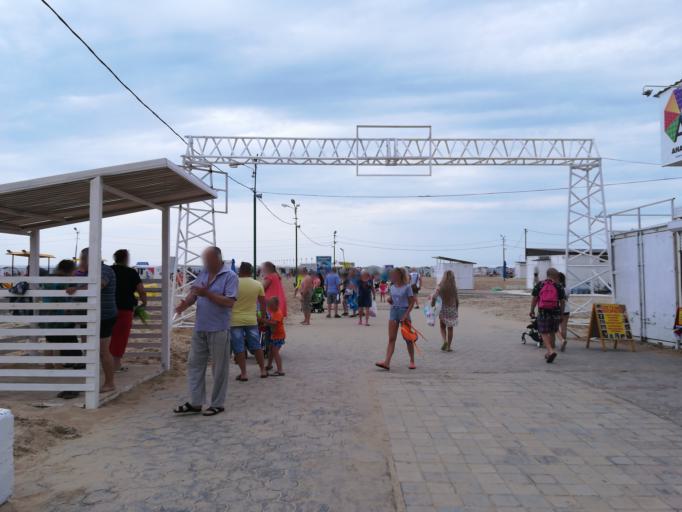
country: RU
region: Krasnodarskiy
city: Vityazevo
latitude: 44.9829
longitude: 37.2497
